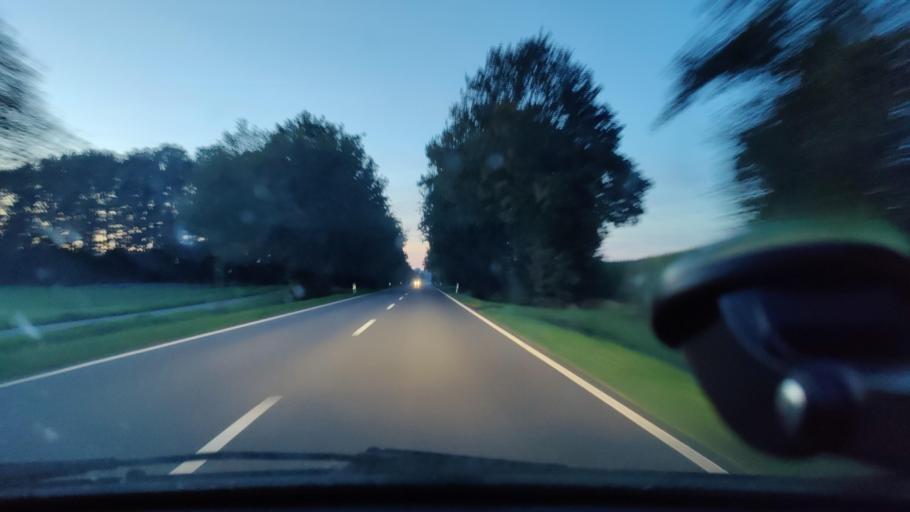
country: DE
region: North Rhine-Westphalia
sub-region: Regierungsbezirk Munster
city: Sudlohn
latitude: 51.8962
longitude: 6.8861
